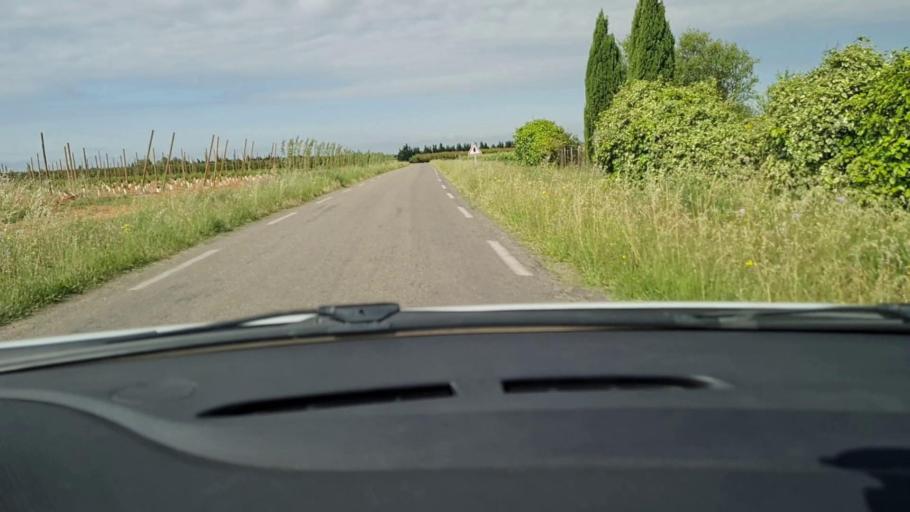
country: FR
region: Languedoc-Roussillon
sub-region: Departement du Gard
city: Jonquieres-Saint-Vincent
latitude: 43.8158
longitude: 4.5523
